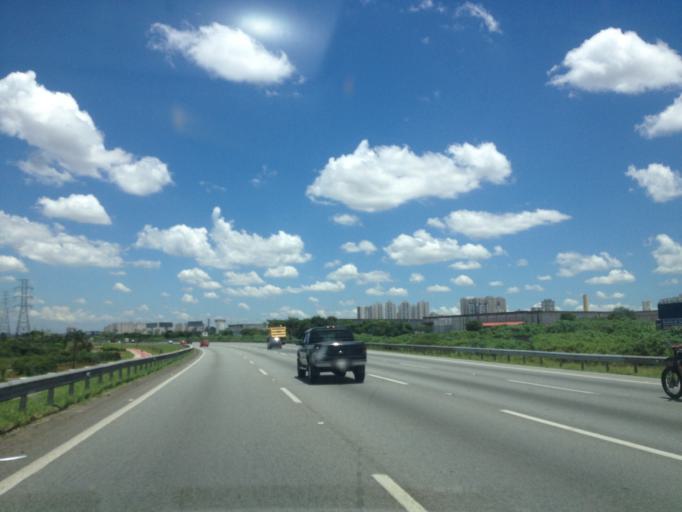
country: BR
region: Sao Paulo
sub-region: Guarulhos
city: Guarulhos
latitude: -23.4808
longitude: -46.5230
